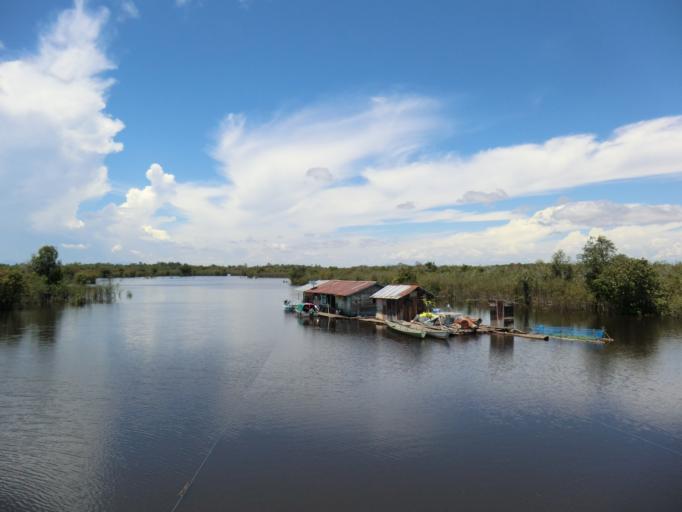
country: MY
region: Sarawak
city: Simanggang
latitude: 0.8918
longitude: 111.9630
